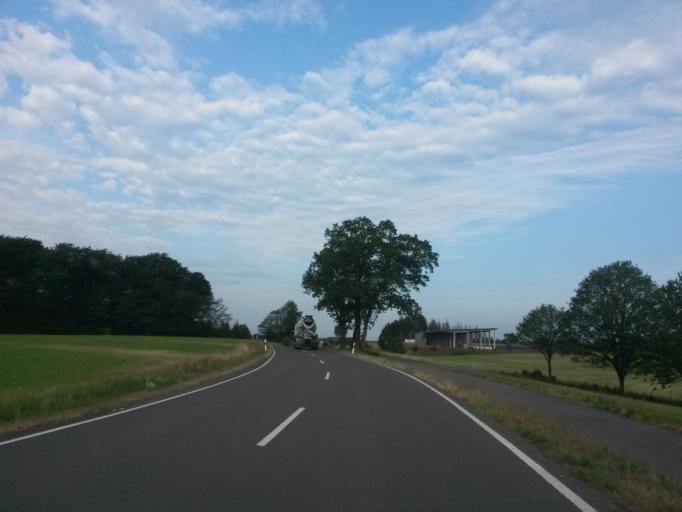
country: DE
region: North Rhine-Westphalia
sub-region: Regierungsbezirk Koln
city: Marienheide
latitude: 51.0922
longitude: 7.5618
